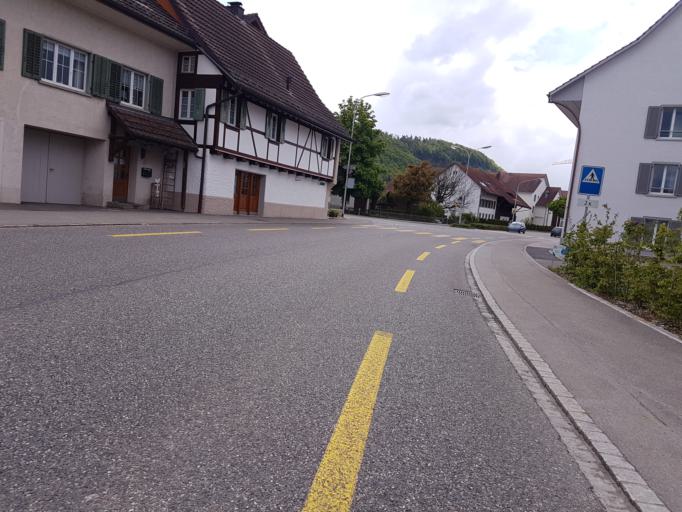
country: CH
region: Aargau
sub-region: Bezirk Baden
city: Wurenlingen
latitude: 47.5344
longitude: 8.2548
